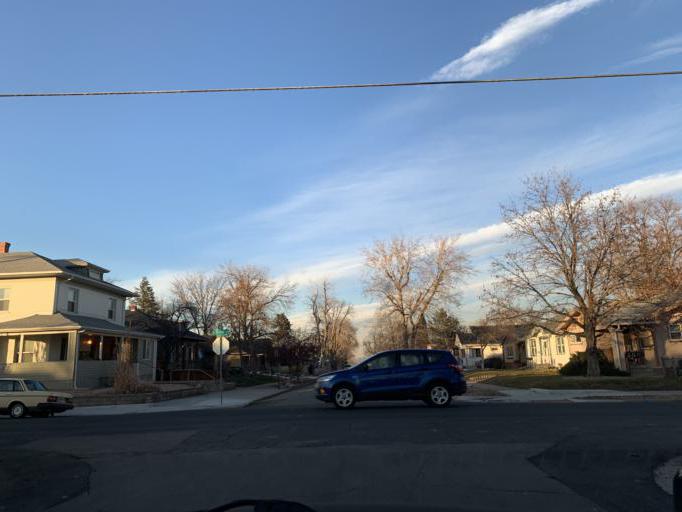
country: US
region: Colorado
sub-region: Adams County
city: Berkley
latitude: 39.7888
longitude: -105.0395
